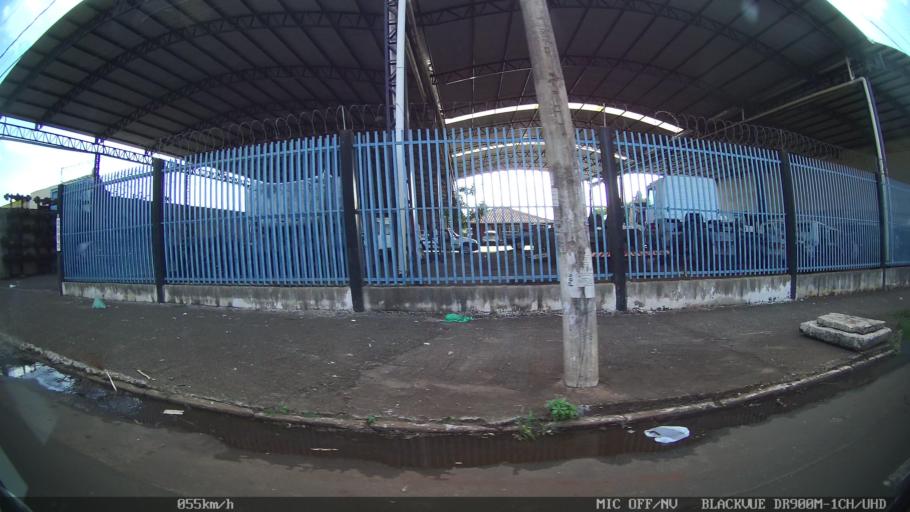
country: BR
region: Sao Paulo
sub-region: Ribeirao Preto
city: Ribeirao Preto
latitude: -21.1463
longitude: -47.7999
